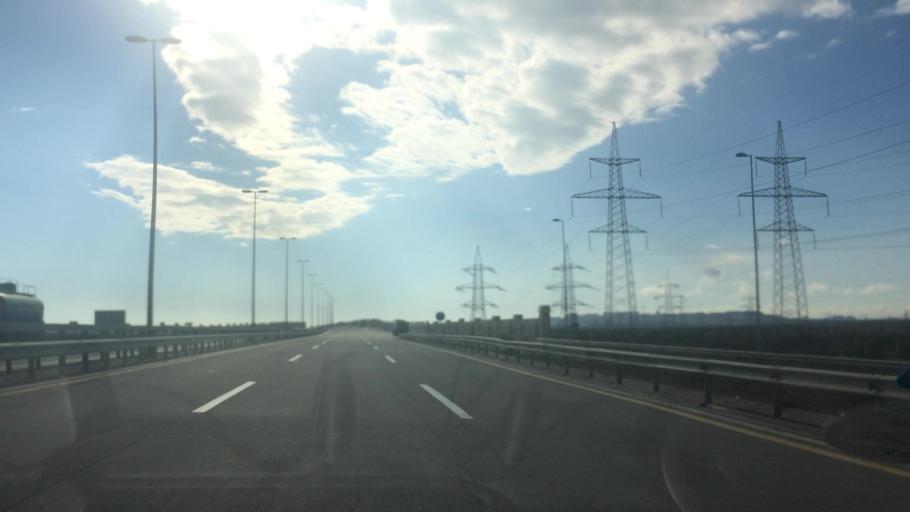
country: AZ
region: Baki
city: Hovsan
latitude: 40.3941
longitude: 50.0786
